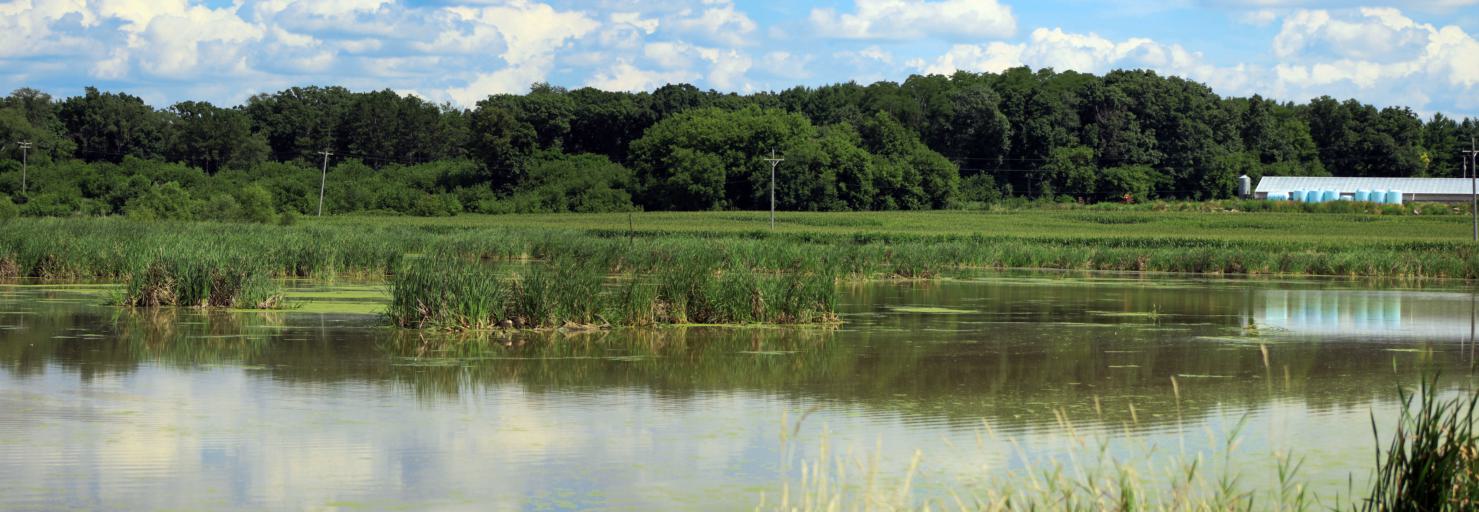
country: US
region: Wisconsin
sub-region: Jefferson County
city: Lake Ripley
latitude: 43.0396
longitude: -88.9885
